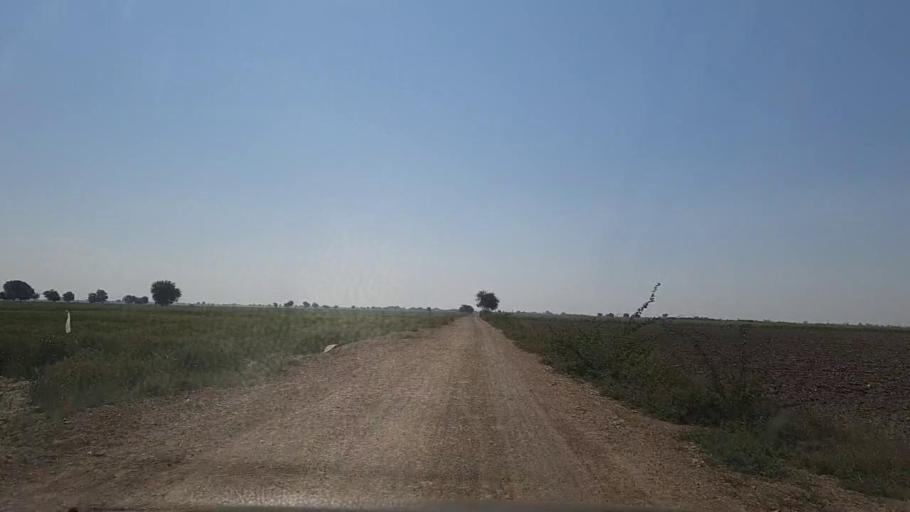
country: PK
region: Sindh
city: Pithoro
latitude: 25.4213
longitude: 69.3798
